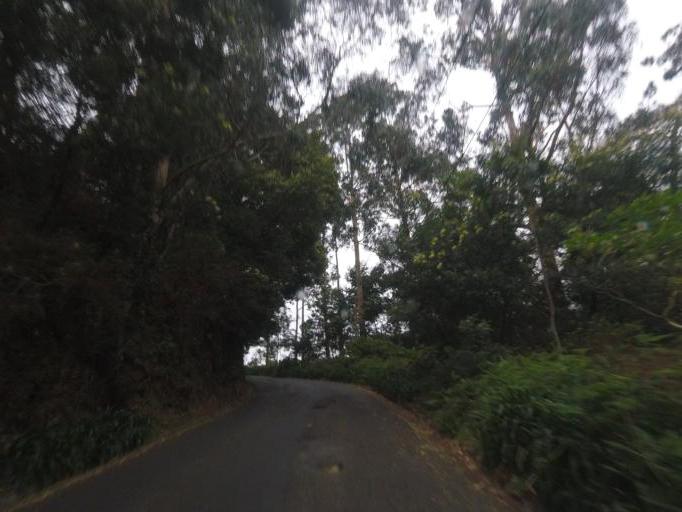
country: PT
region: Madeira
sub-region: Santa Cruz
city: Santa Cruz
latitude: 32.7306
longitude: -16.8227
